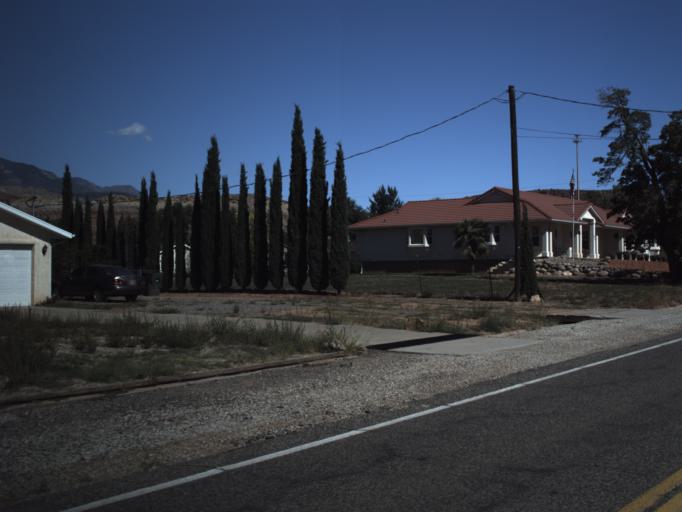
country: US
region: Utah
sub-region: Washington County
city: Toquerville
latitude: 37.2314
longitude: -113.3692
